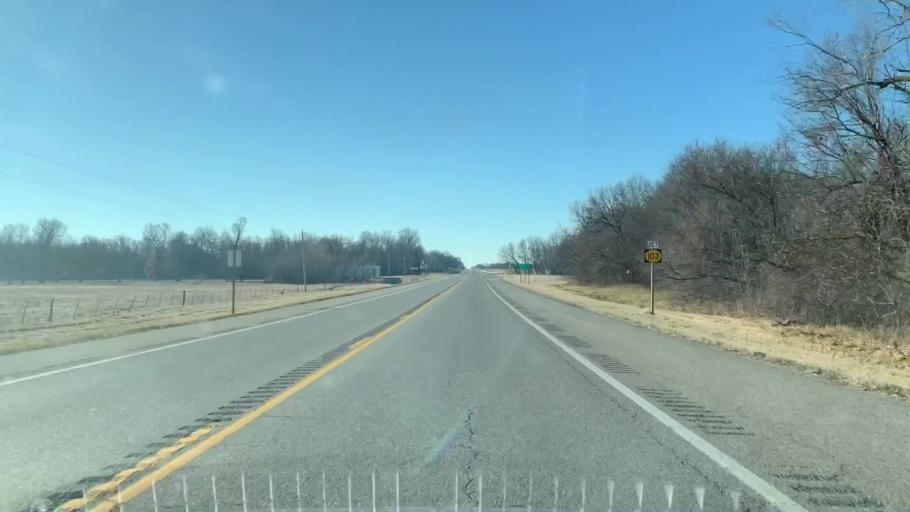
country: US
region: Kansas
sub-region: Crawford County
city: Pittsburg
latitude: 37.3122
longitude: -94.7055
